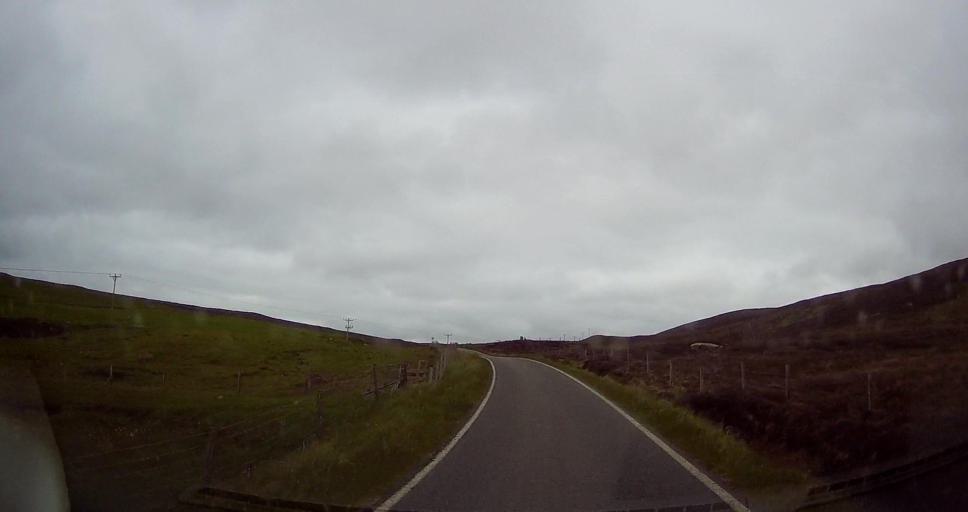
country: GB
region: Scotland
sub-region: Shetland Islands
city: Lerwick
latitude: 60.3064
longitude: -1.3379
